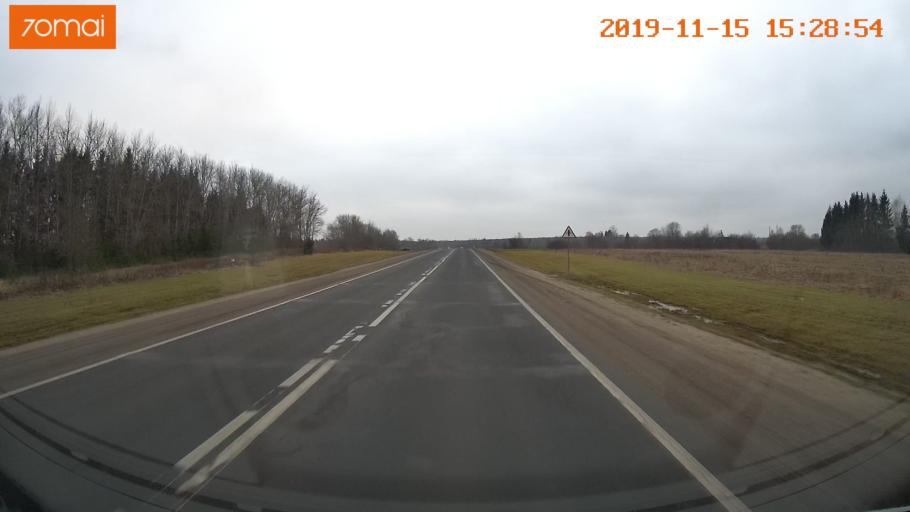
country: RU
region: Jaroslavl
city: Danilov
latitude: 58.1269
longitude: 40.1280
